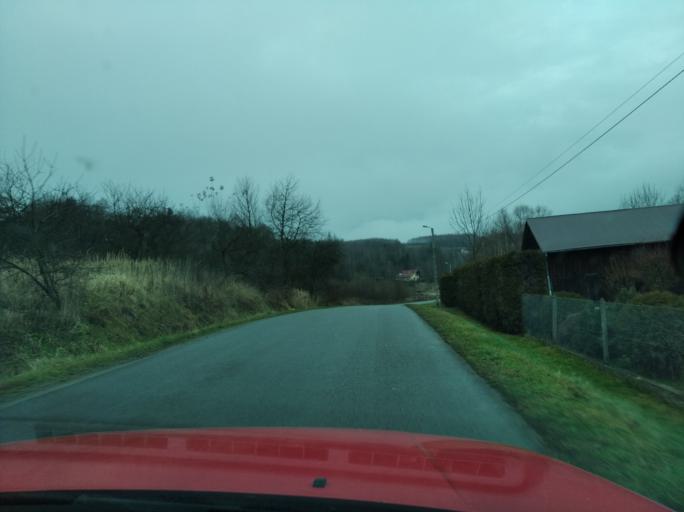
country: PL
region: Subcarpathian Voivodeship
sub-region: Powiat przemyski
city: Nienadowa
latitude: 49.8503
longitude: 22.4269
